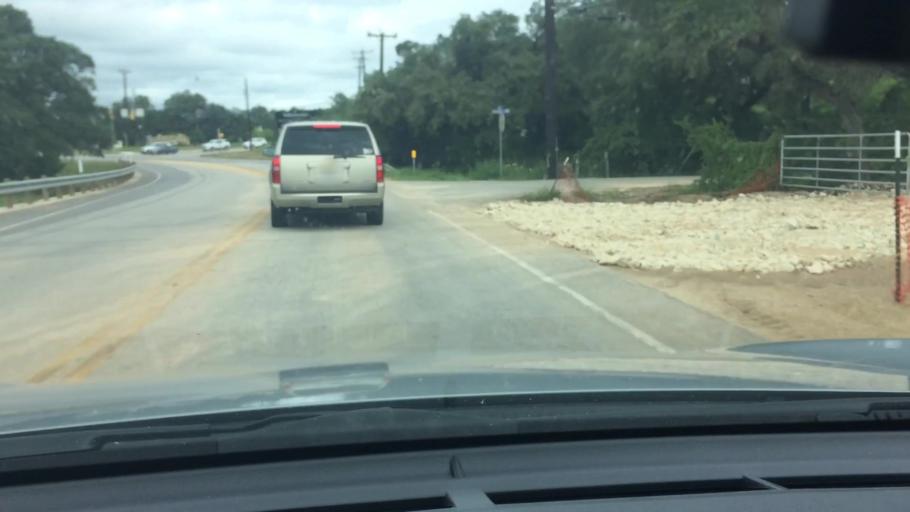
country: US
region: Texas
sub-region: Comal County
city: Garden Ridge
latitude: 29.6395
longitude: -98.3776
